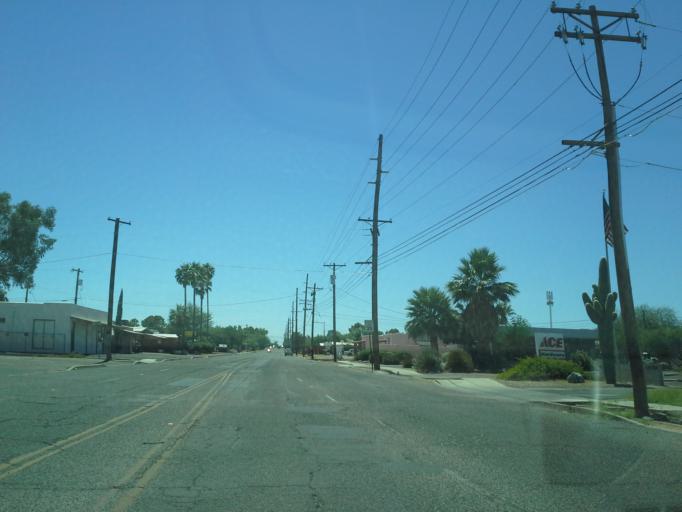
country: US
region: Arizona
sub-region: Pima County
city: Tucson
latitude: 32.2495
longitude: -110.9269
